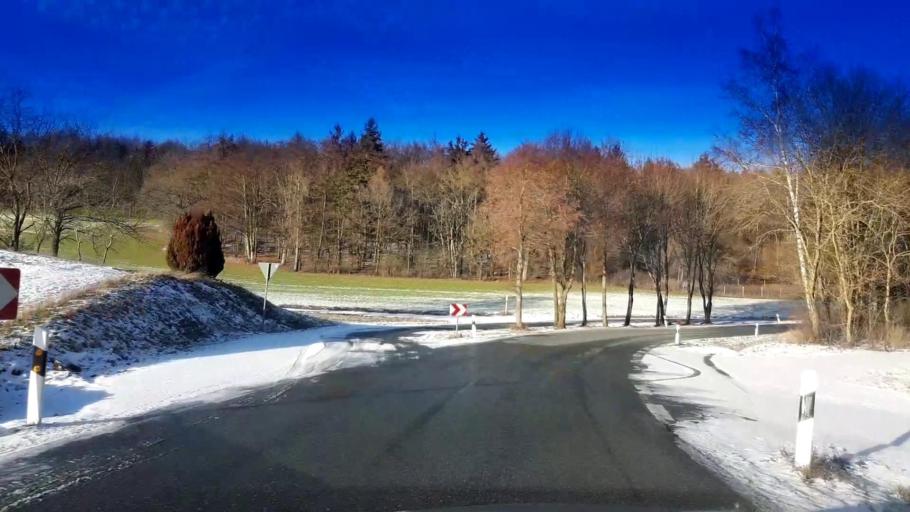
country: DE
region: Bavaria
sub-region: Upper Franconia
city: Heiligenstadt
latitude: 49.8521
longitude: 11.1447
